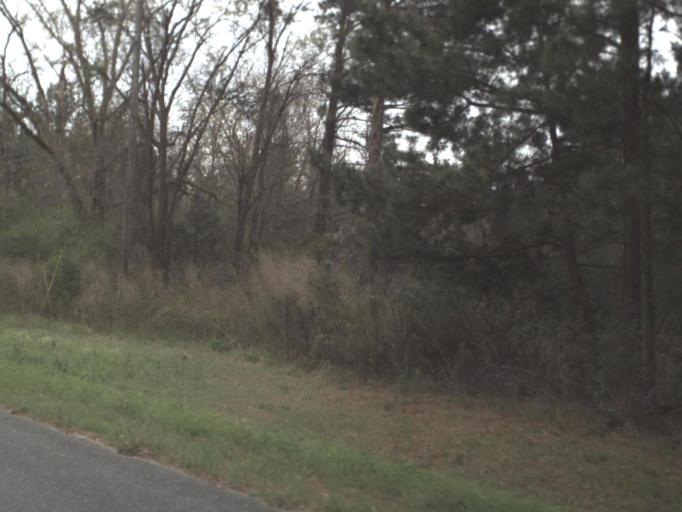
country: US
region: Florida
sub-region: Calhoun County
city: Blountstown
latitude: 30.4765
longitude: -85.2002
